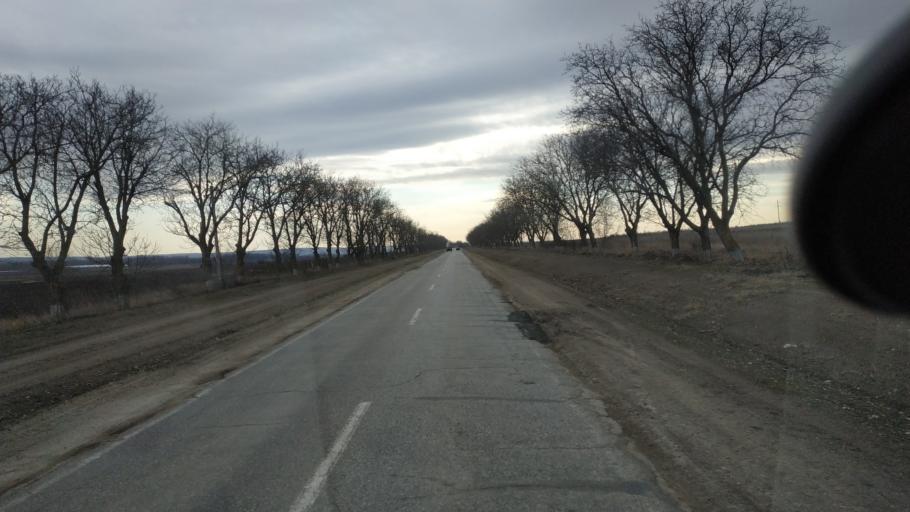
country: MD
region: Criuleni
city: Criuleni
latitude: 47.1827
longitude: 29.1386
